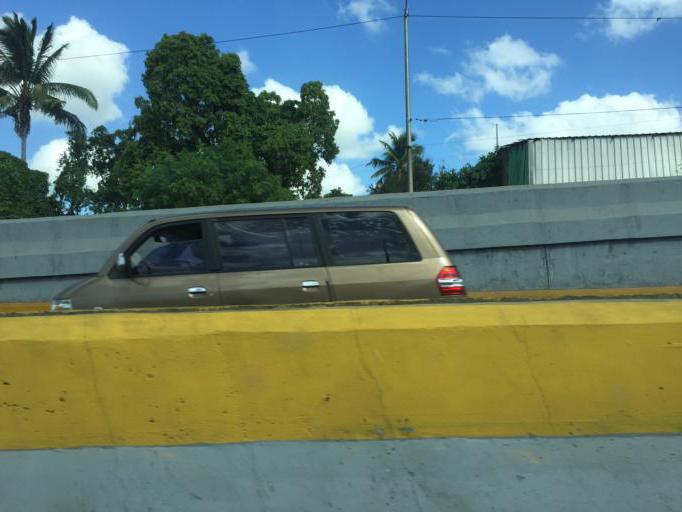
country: DO
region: Santo Domingo
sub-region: Santo Domingo
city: Santo Domingo Este
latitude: 18.4856
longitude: -69.8739
